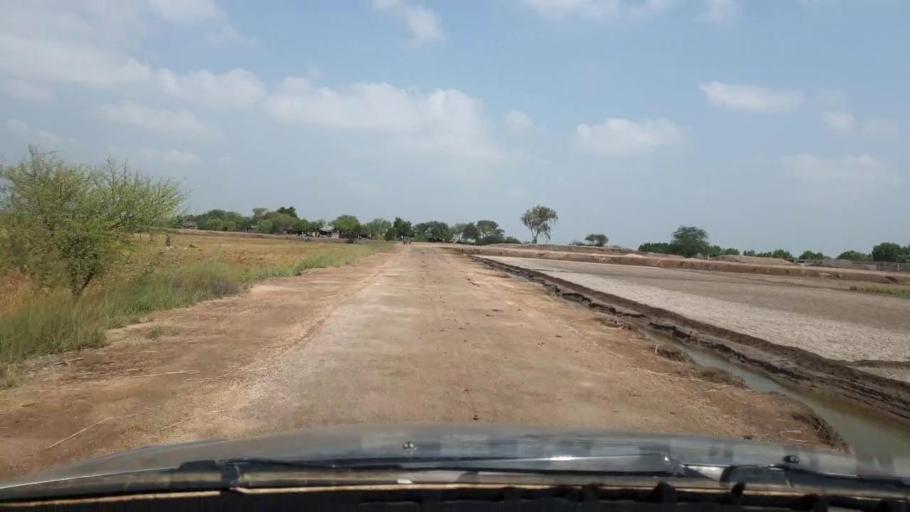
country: PK
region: Sindh
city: Matli
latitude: 25.0935
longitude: 68.6915
